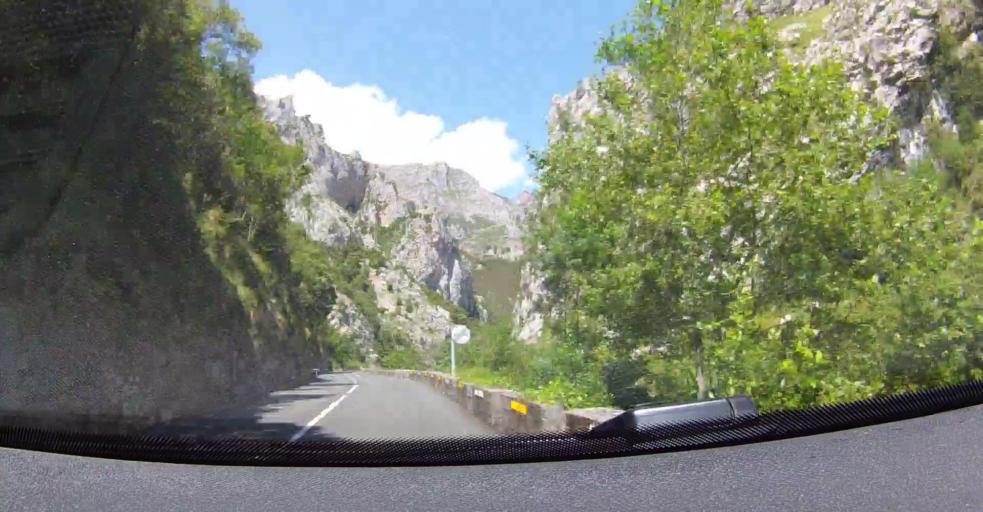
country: ES
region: Cantabria
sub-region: Provincia de Cantabria
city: Tresviso
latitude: 43.2693
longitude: -4.6353
